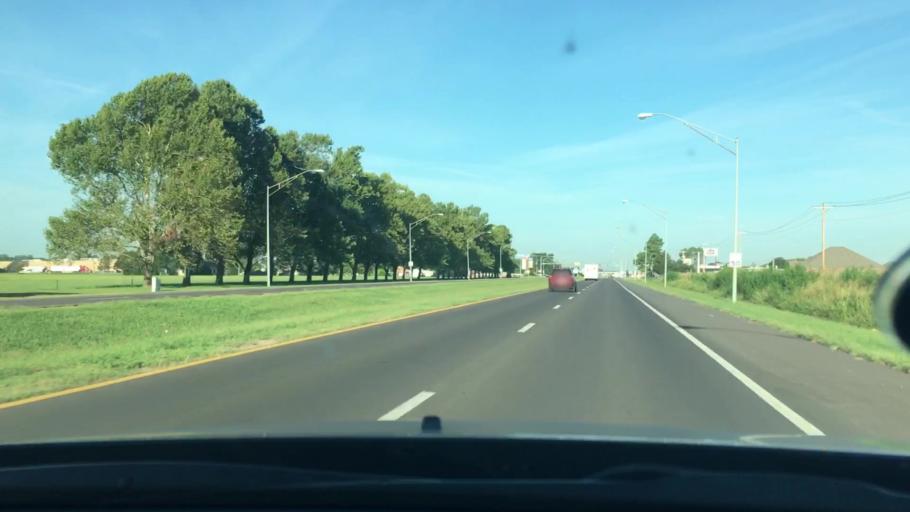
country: US
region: Oklahoma
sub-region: Garvin County
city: Pauls Valley
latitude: 34.7391
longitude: -97.2430
